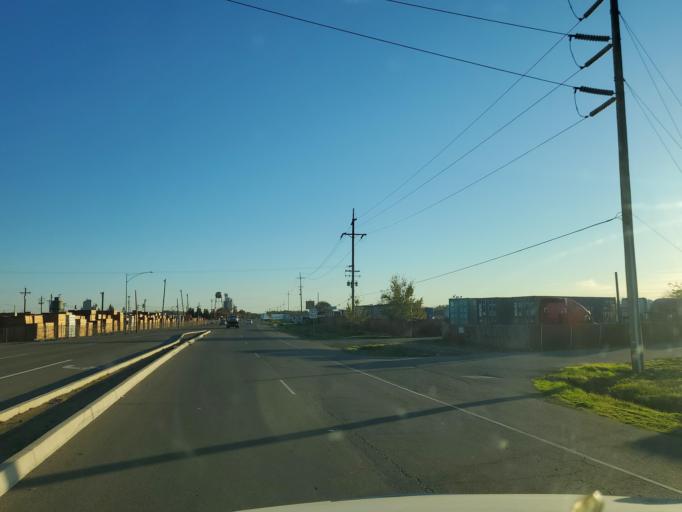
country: US
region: California
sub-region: San Joaquin County
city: Taft Mosswood
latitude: 37.9105
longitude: -121.2758
